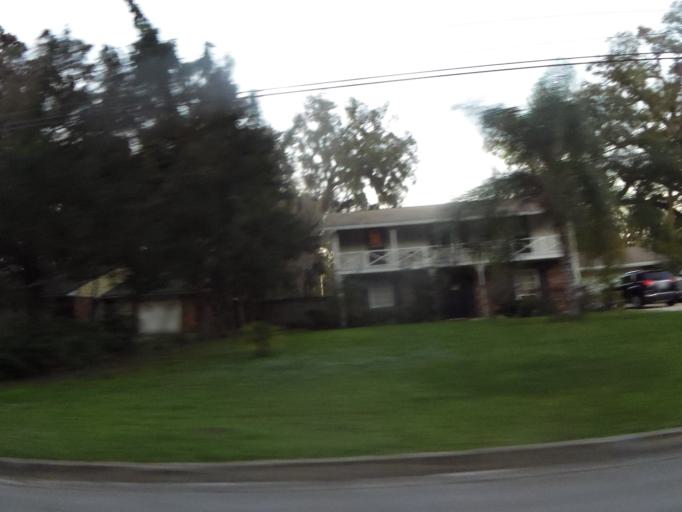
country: US
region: Florida
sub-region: Clay County
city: Orange Park
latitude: 30.1581
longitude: -81.7016
